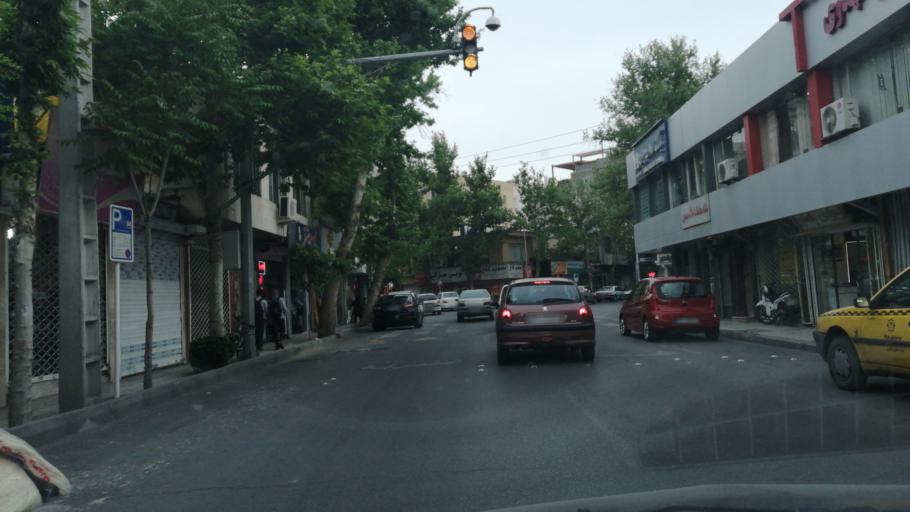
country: IR
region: Razavi Khorasan
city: Mashhad
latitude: 36.2965
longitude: 59.5822
